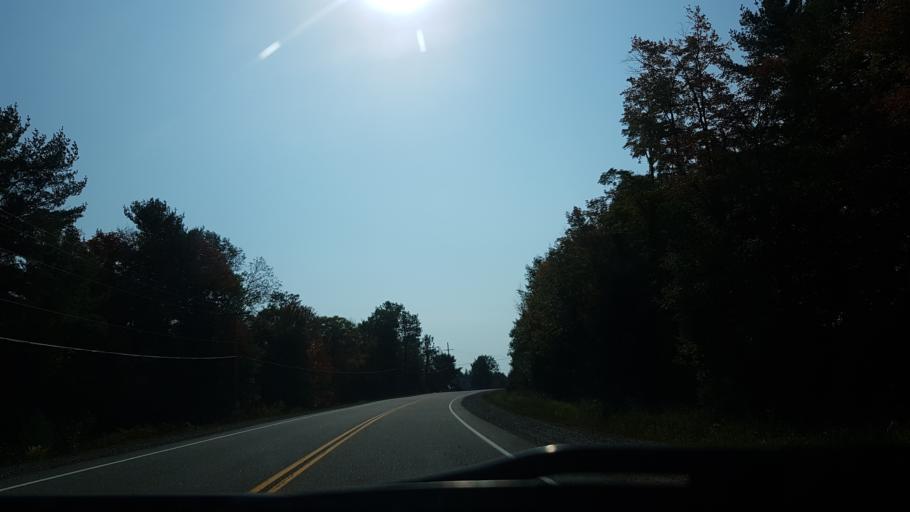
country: CA
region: Ontario
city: Bracebridge
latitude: 44.9887
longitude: -79.2775
